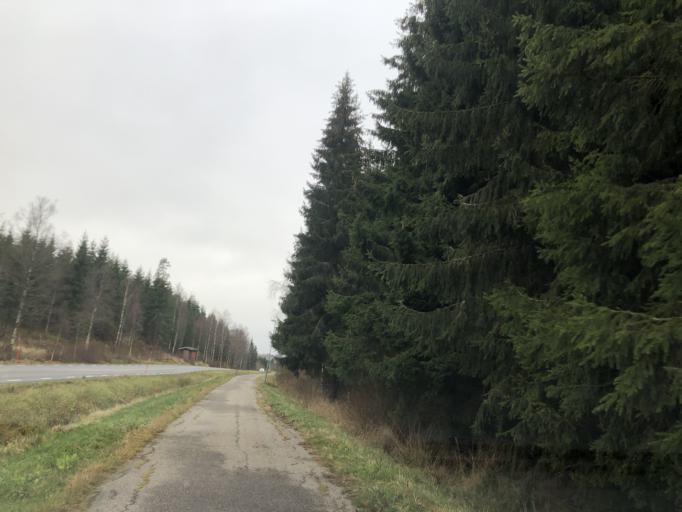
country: SE
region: Vaestra Goetaland
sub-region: Ulricehamns Kommun
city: Ulricehamn
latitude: 57.6738
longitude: 13.4498
